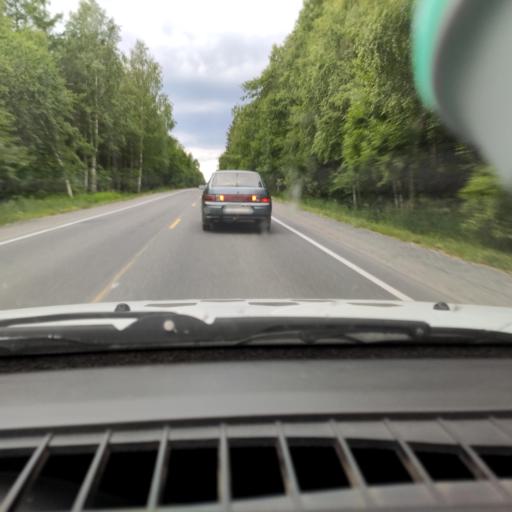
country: RU
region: Chelyabinsk
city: Syrostan
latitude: 55.1190
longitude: 59.8334
